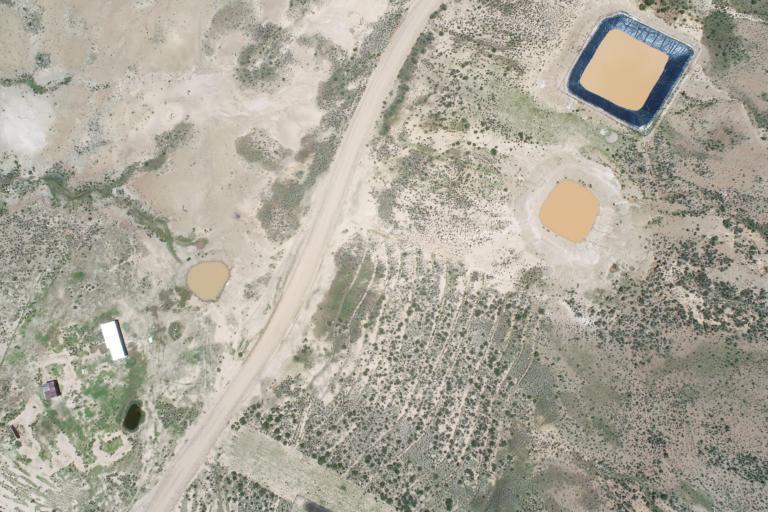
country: BO
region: La Paz
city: Curahuara de Carangas
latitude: -17.3078
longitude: -68.4944
